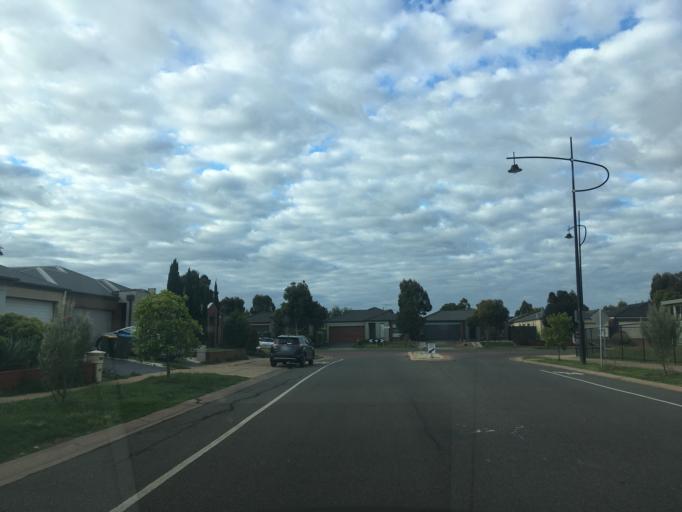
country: AU
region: Victoria
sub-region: Wyndham
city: Hoppers Crossing
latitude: -37.8935
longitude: 144.7243
